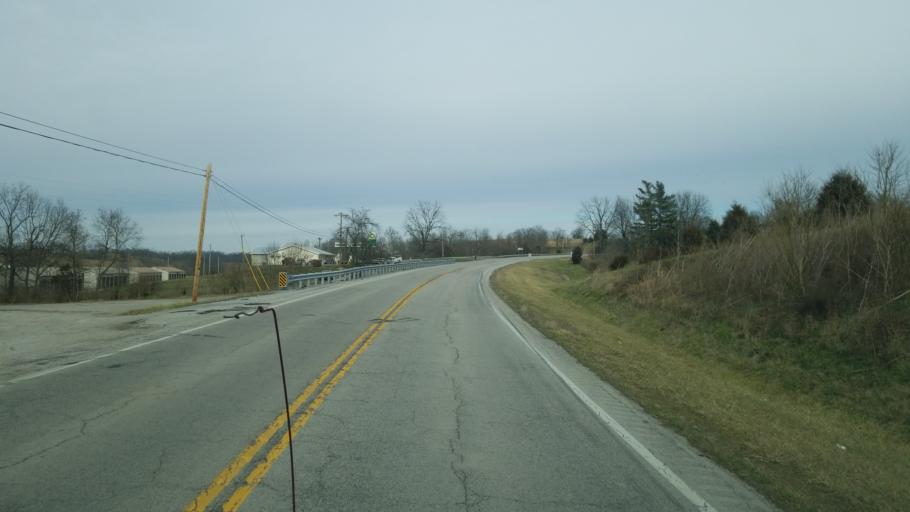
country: US
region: Kentucky
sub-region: Robertson County
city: Mount Olivet
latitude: 38.4358
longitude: -83.9912
